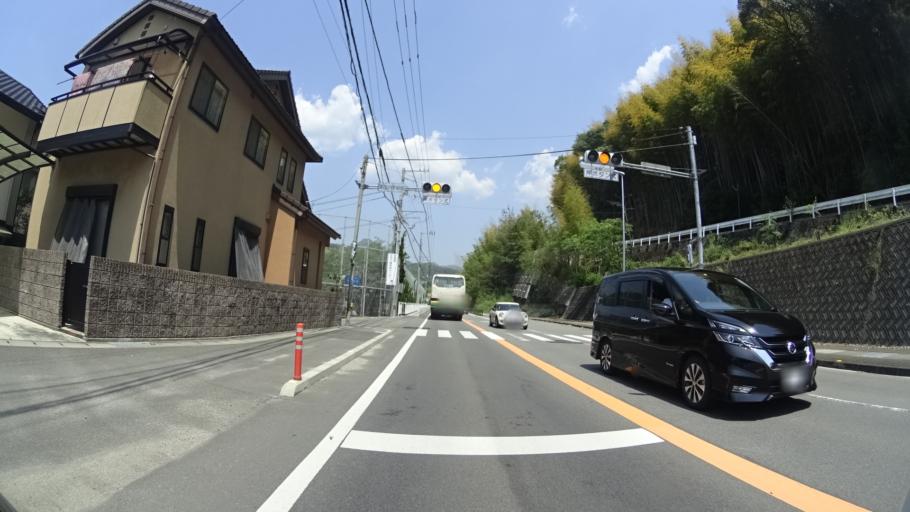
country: JP
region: Ehime
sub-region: Shikoku-chuo Shi
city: Matsuyama
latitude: 33.8601
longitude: 132.8143
